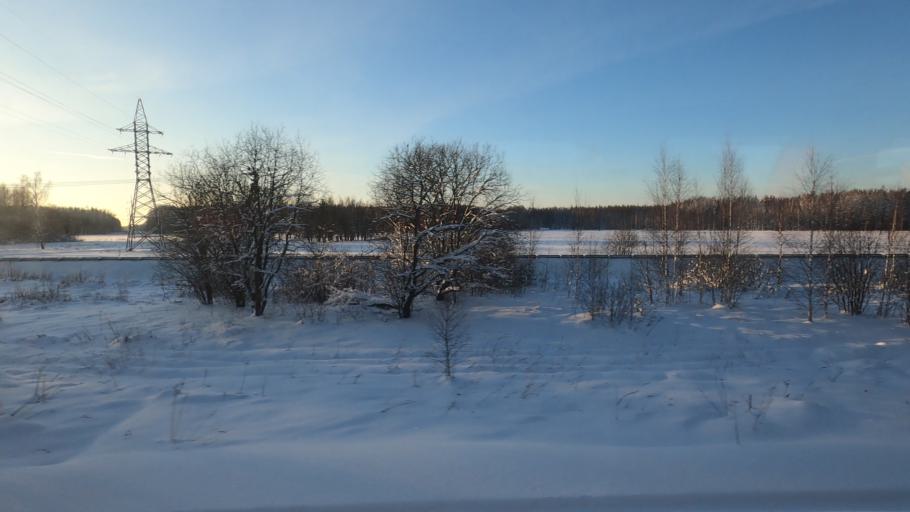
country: RU
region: Moskovskaya
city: Novo-Nikol'skoye
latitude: 56.6445
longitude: 37.5627
